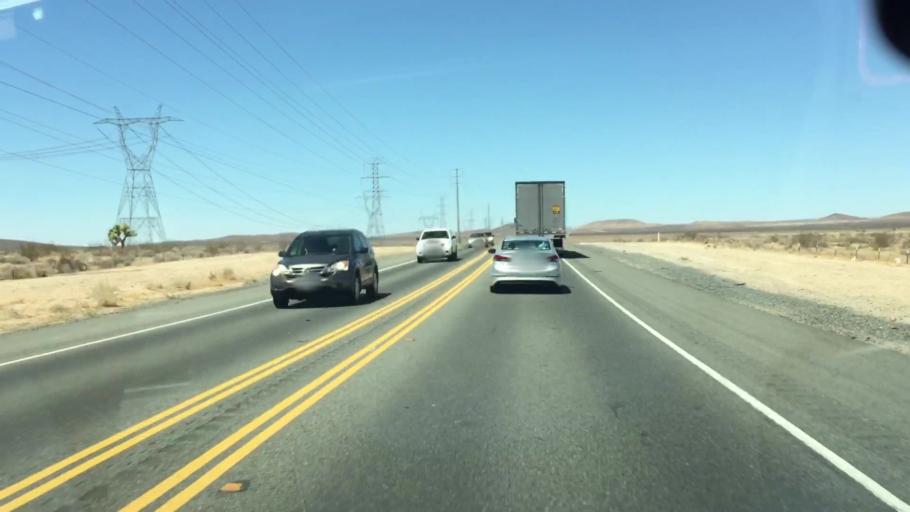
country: US
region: California
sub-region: San Bernardino County
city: Adelanto
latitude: 34.8037
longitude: -117.4887
